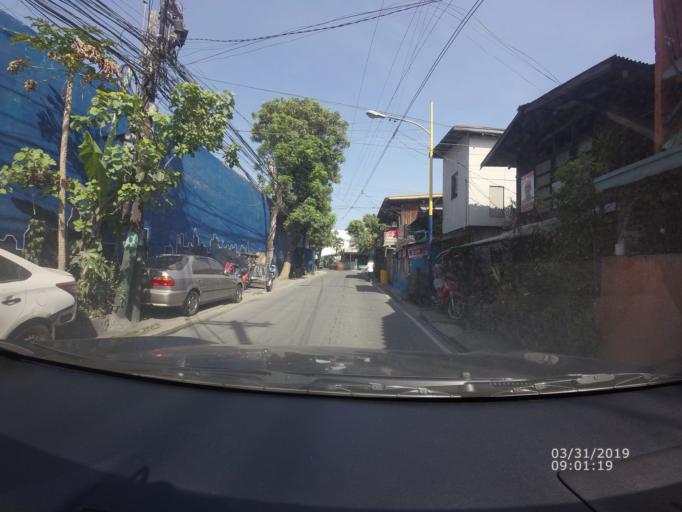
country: PH
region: Metro Manila
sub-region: Mandaluyong
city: Mandaluyong City
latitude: 14.5762
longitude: 121.0246
